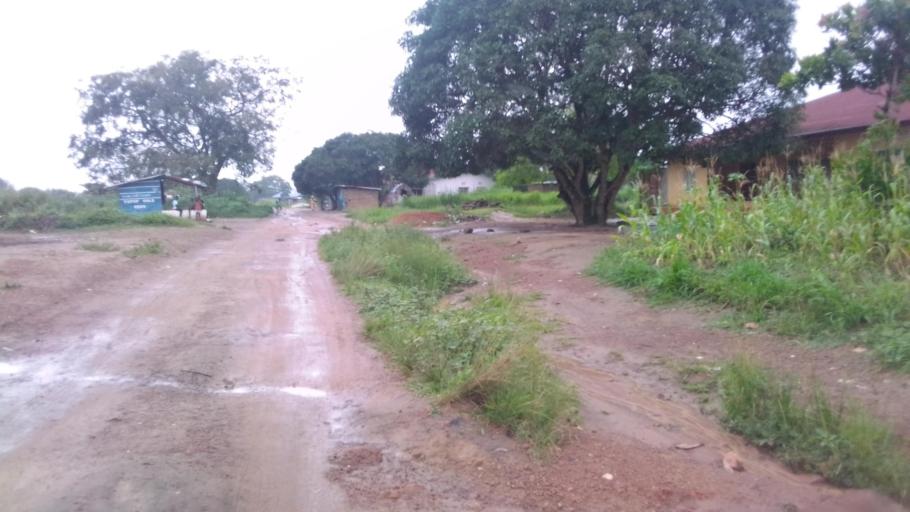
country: SL
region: Eastern Province
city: Kenema
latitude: 7.9017
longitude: -11.1677
